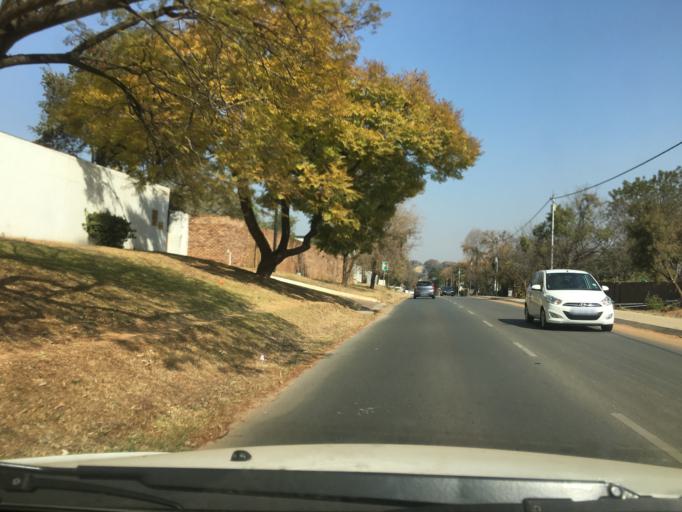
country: ZA
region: Gauteng
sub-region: City of Johannesburg Metropolitan Municipality
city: Midrand
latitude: -26.0628
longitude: 28.0548
